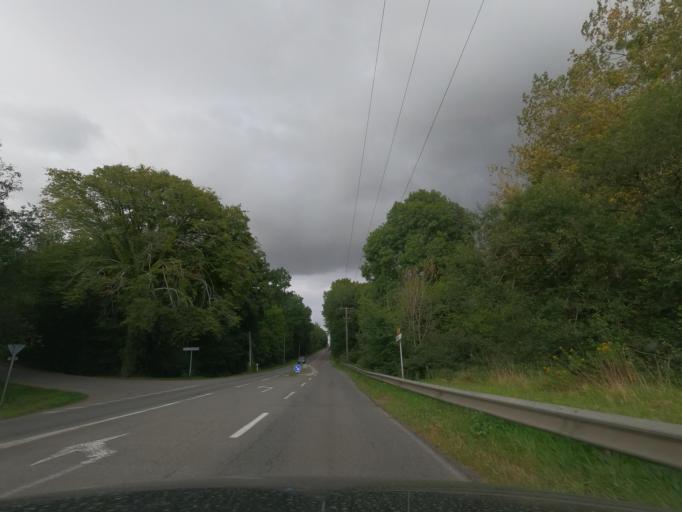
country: FR
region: Haute-Normandie
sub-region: Departement de l'Eure
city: Menneval
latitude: 49.1216
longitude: 0.6300
